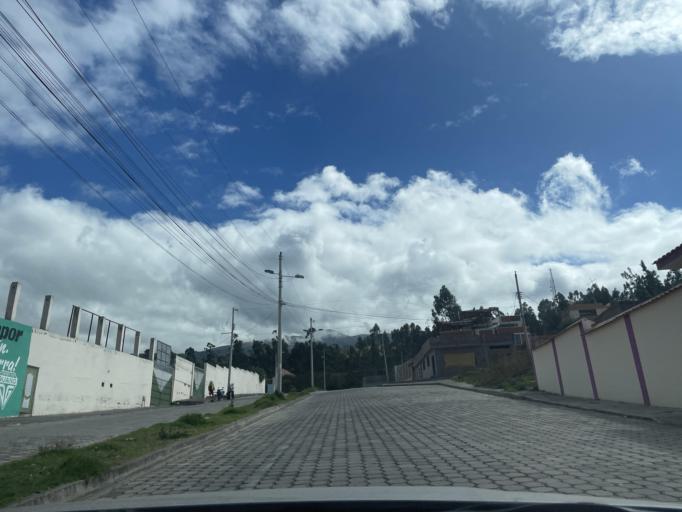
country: EC
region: Chimborazo
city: Guano
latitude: -1.6024
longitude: -78.6426
